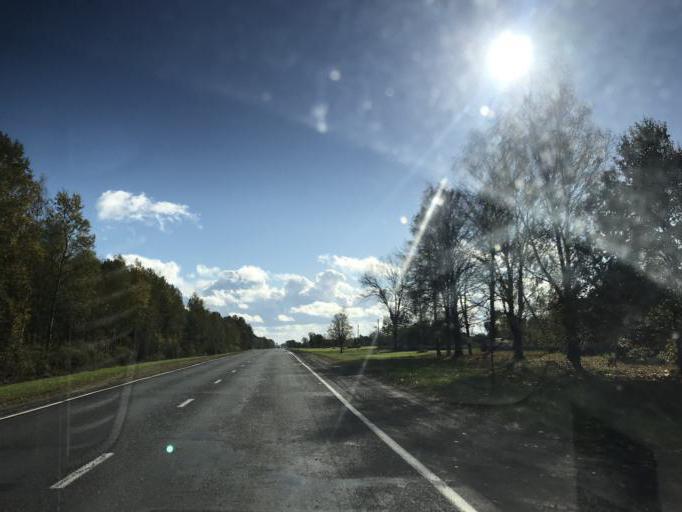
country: BY
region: Gomel
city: Dowsk
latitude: 53.0523
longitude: 30.5436
